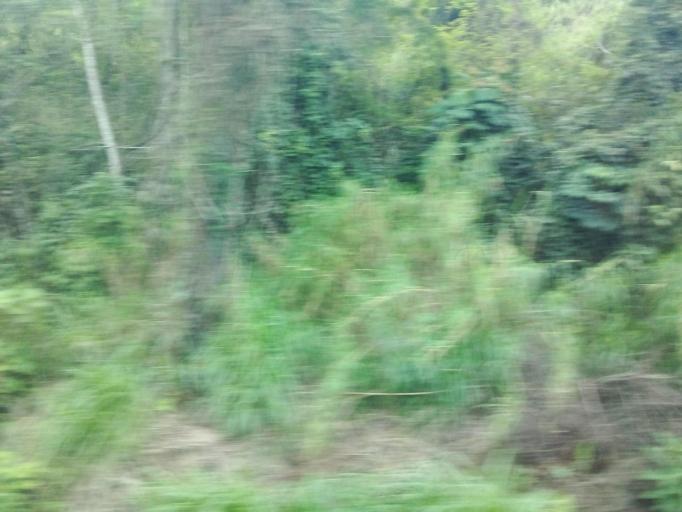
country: BR
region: Minas Gerais
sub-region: Rio Piracicaba
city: Rio Piracicaba
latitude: -19.8883
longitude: -43.1326
